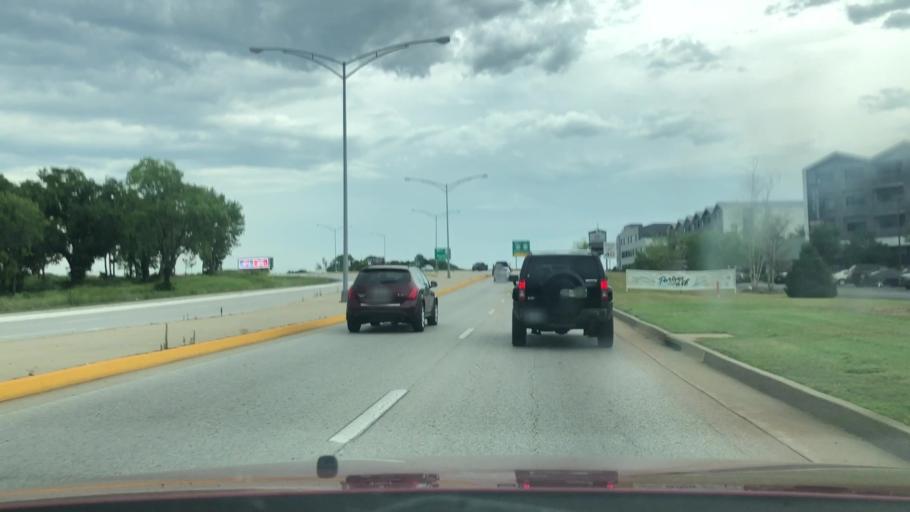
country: US
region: Missouri
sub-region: Greene County
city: Springfield
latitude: 37.1371
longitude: -93.2560
